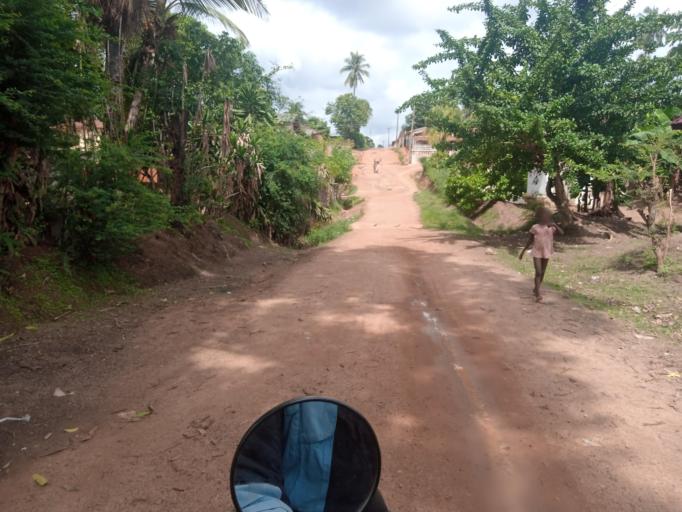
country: SL
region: Southern Province
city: Bo
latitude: 7.9735
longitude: -11.7334
